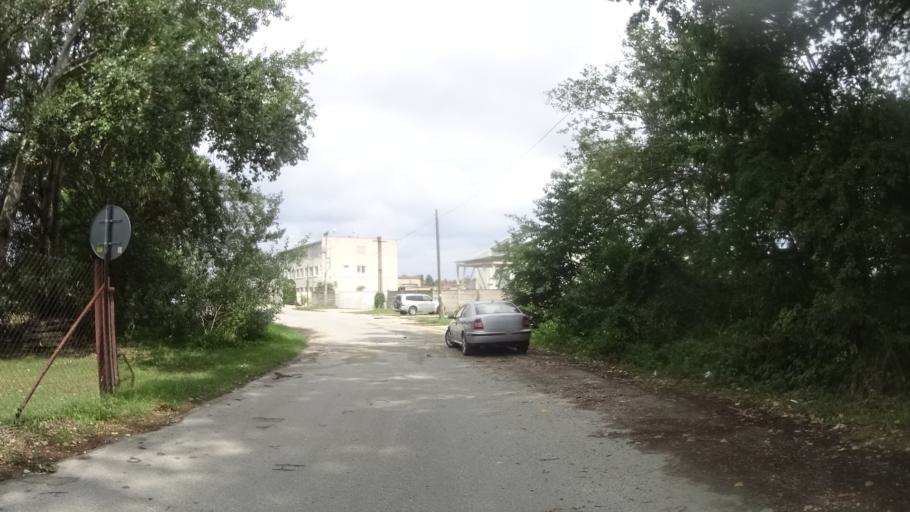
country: HU
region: Gyor-Moson-Sopron
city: Bony
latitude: 47.7464
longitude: 17.8780
